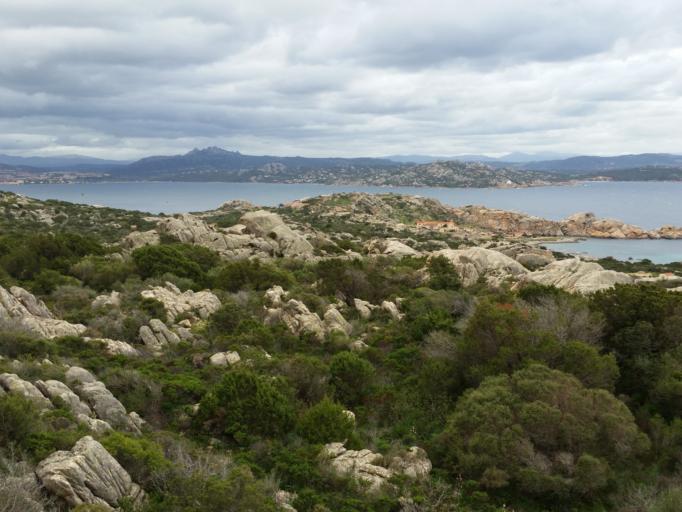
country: IT
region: Sardinia
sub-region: Provincia di Olbia-Tempio
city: La Maddalena
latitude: 41.2263
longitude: 9.3843
